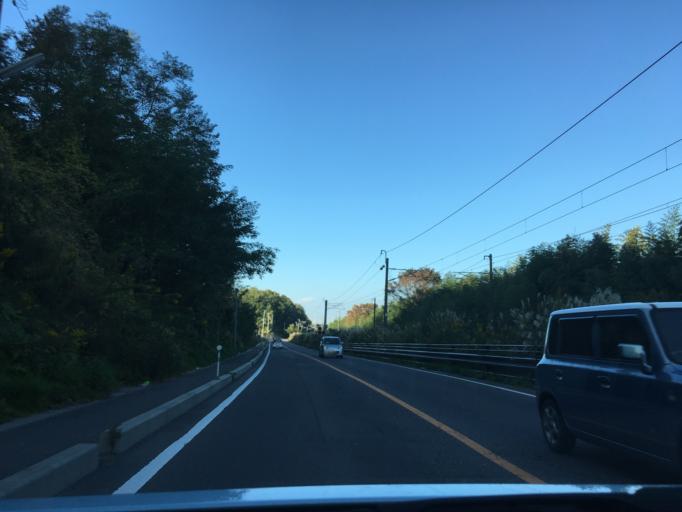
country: JP
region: Fukushima
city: Sukagawa
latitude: 37.3127
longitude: 140.3777
